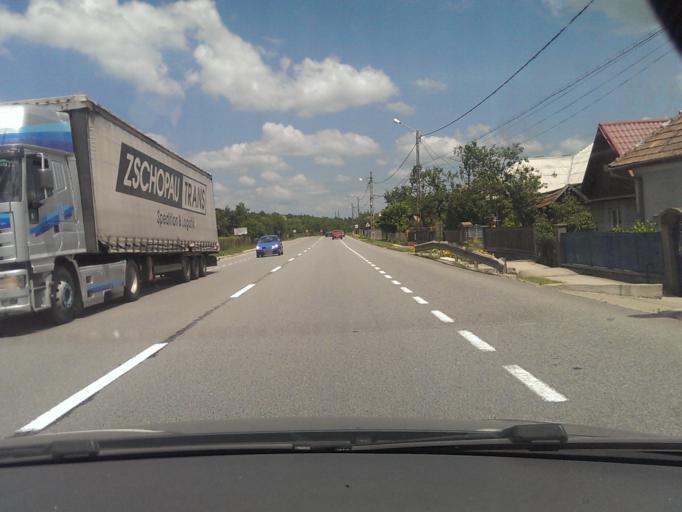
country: RO
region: Cluj
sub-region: Comuna Bontida
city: Rascruci
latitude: 46.9113
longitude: 23.7761
